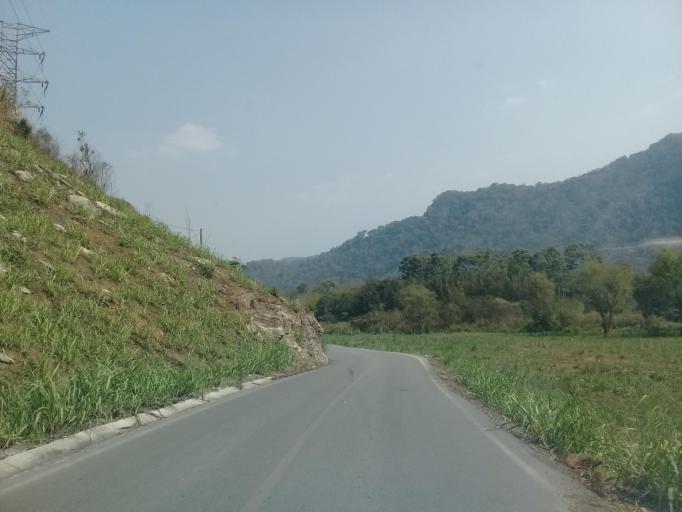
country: MX
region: Veracruz
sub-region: Ixtaczoquitlan
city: Campo Chico
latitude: 18.8292
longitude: -97.0107
